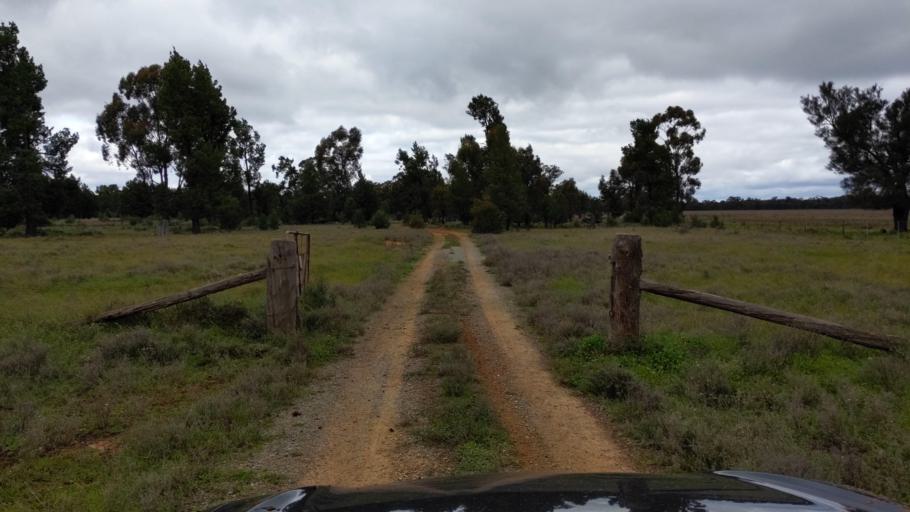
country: AU
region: New South Wales
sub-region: Coolamon
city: Coolamon
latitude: -34.8561
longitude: 146.9180
